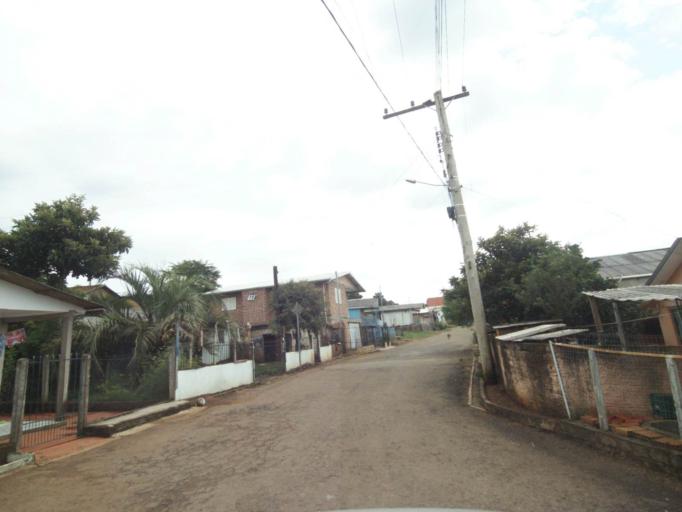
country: BR
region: Rio Grande do Sul
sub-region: Lagoa Vermelha
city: Lagoa Vermelha
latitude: -28.2263
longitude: -51.5149
